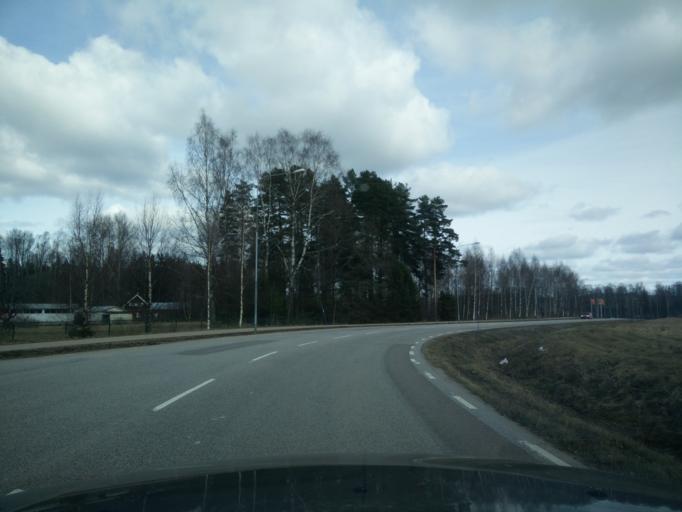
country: SE
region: Vaermland
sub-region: Hagfors Kommun
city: Hagfors
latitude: 60.0083
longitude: 13.5950
